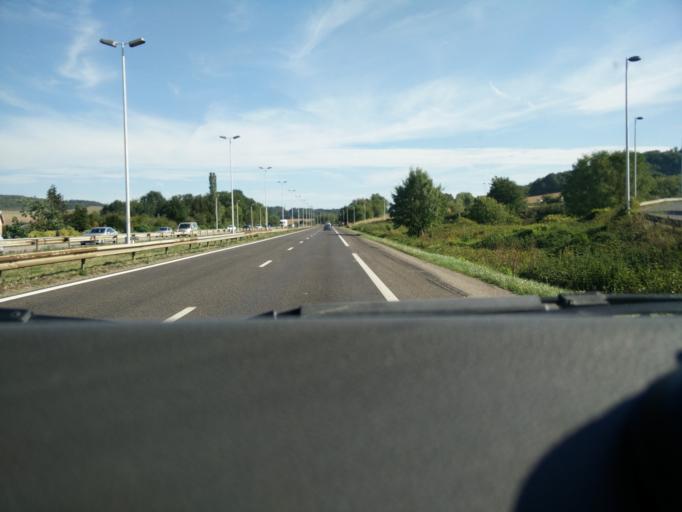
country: FR
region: Lorraine
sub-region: Departement de Meurthe-et-Moselle
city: Belleville
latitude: 48.8177
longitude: 6.1085
